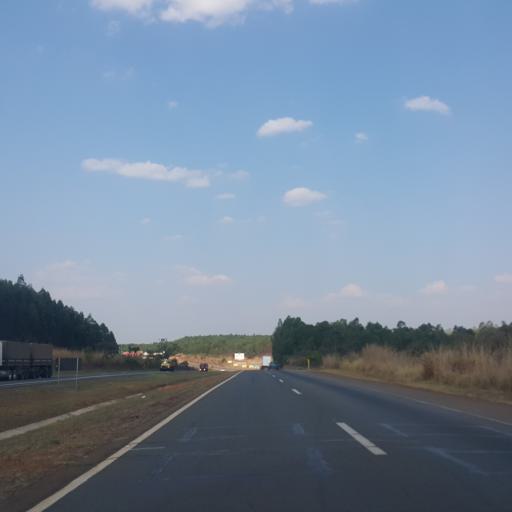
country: BR
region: Goias
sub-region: Abadiania
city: Abadiania
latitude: -16.1894
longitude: -48.6819
